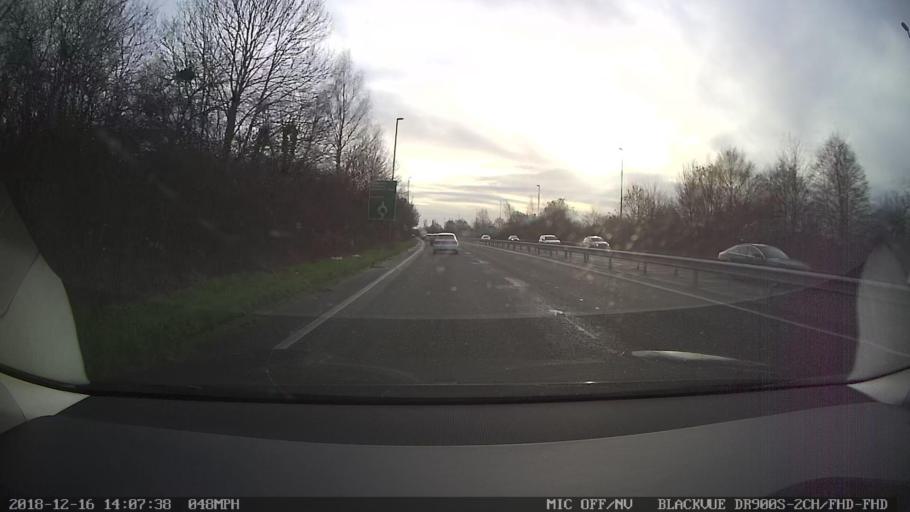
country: GB
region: England
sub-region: Borough of Stockport
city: Cheadle Hulme
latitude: 53.3698
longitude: -2.2105
